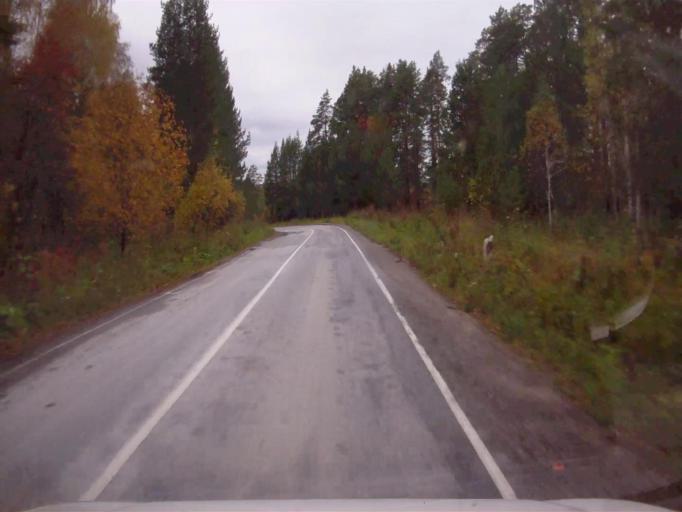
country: RU
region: Chelyabinsk
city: Nyazepetrovsk
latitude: 56.0565
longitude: 59.4711
